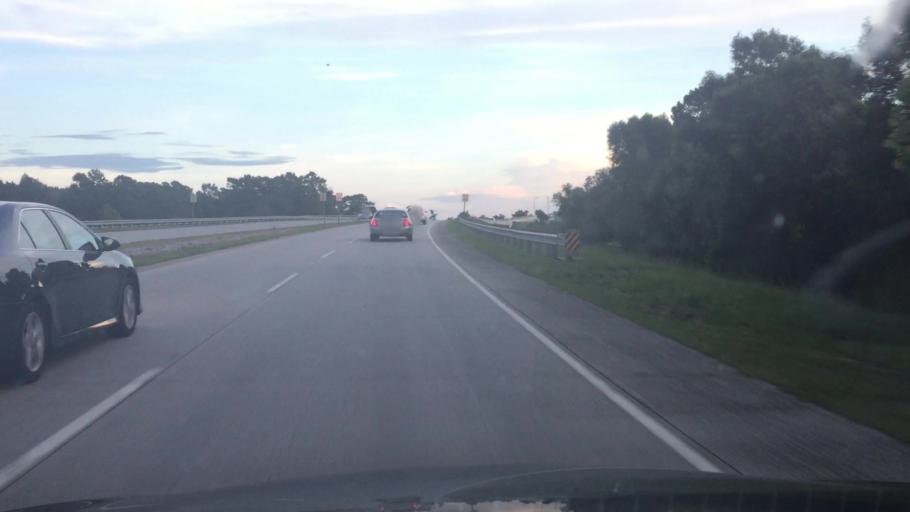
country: US
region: South Carolina
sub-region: Horry County
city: North Myrtle Beach
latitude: 33.8371
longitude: -78.6891
